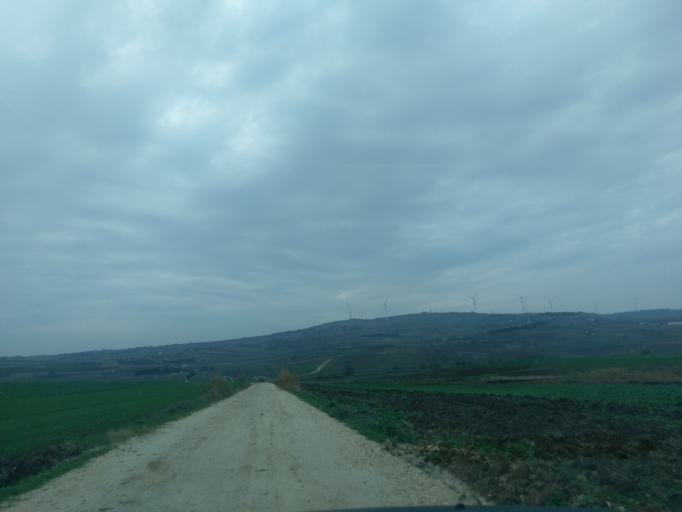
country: TR
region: Istanbul
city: Canta
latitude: 41.1102
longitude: 28.1032
